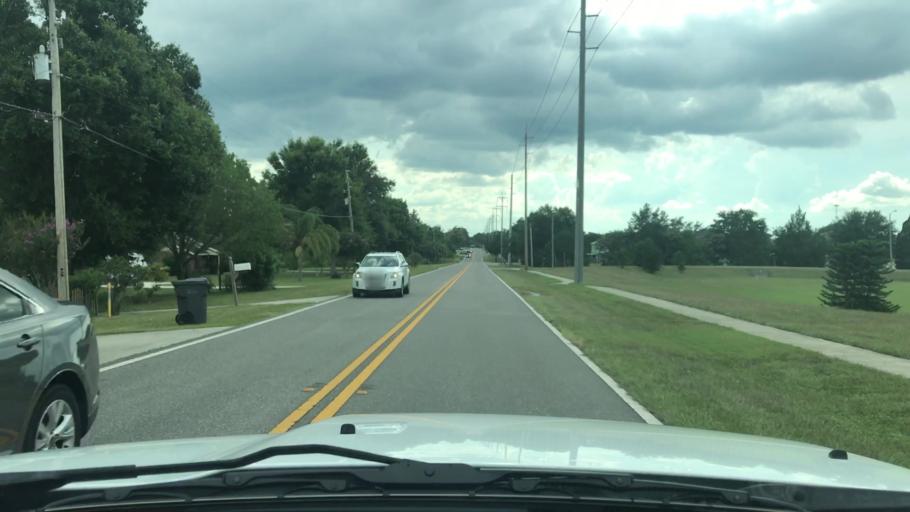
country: US
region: Florida
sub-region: Polk County
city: Cypress Gardens
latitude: 28.0151
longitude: -81.6657
